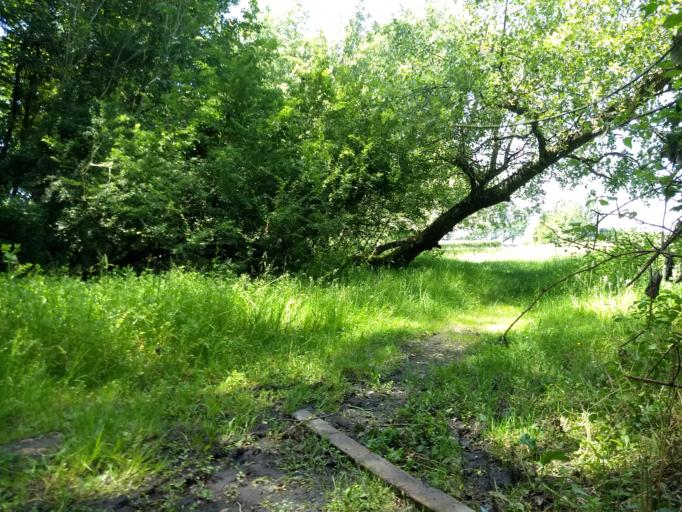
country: GB
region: England
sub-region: Isle of Wight
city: Shalfleet
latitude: 50.6785
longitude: -1.4037
